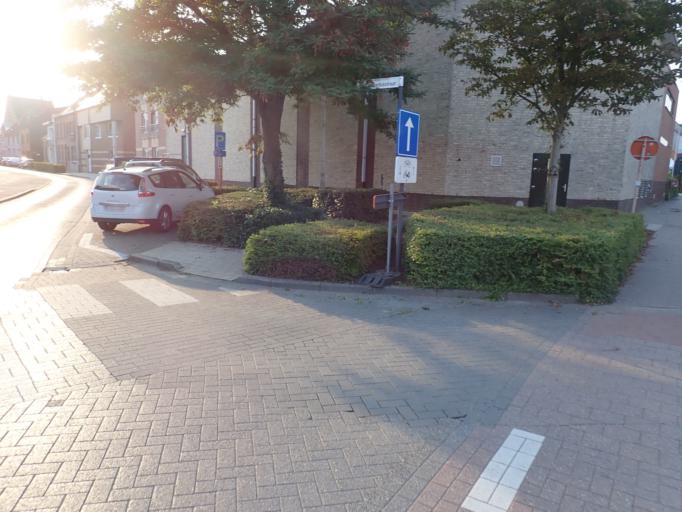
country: BE
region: Flanders
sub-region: Provincie Antwerpen
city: Berlaar
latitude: 51.1391
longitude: 4.6326
